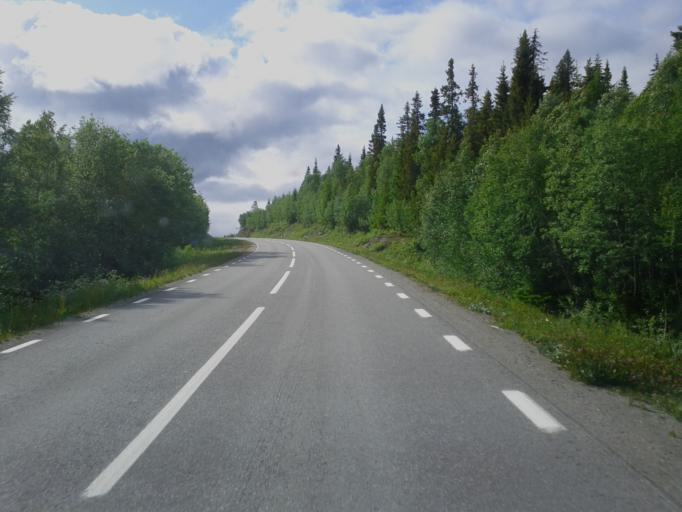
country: NO
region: Nordland
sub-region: Rana
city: Mo i Rana
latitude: 65.7113
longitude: 15.2291
